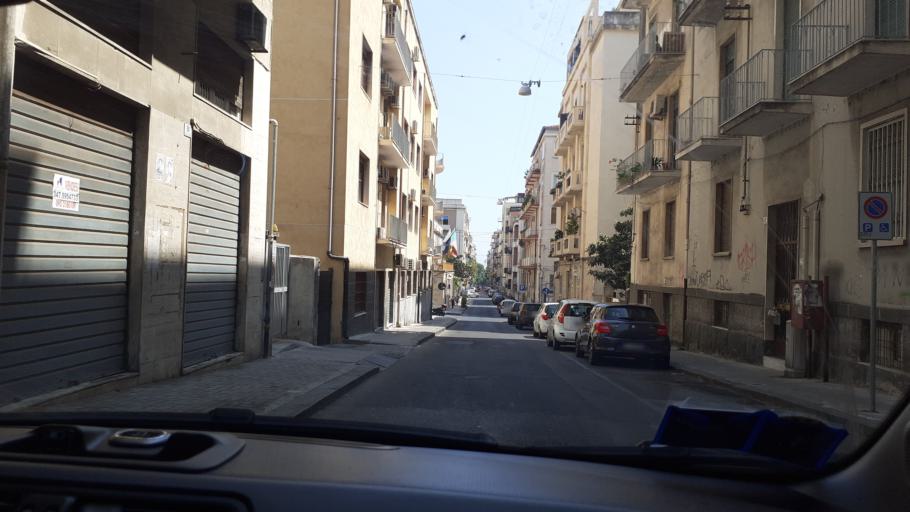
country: IT
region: Sicily
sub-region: Catania
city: Catania
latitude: 37.5095
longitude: 15.0755
